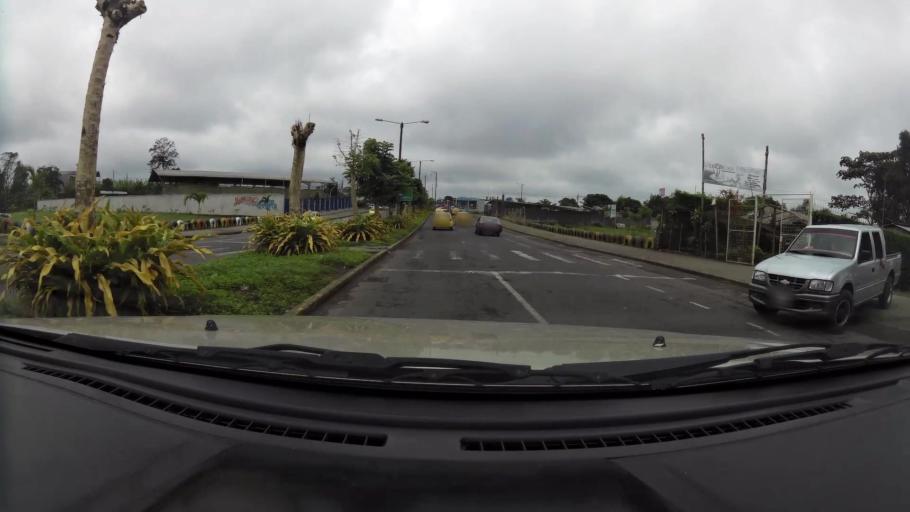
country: EC
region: Santo Domingo de los Tsachilas
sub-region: Canton Santo Domingo de los Colorados
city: Santo Domingo de los Colorados
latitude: -0.2626
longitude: -79.1787
